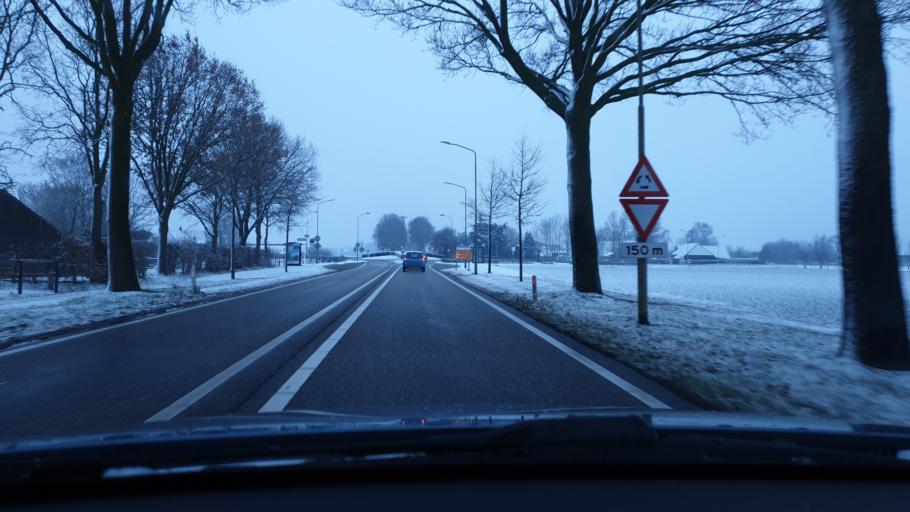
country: NL
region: North Brabant
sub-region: Gemeente Landerd
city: Zeeland
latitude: 51.7091
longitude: 5.6687
